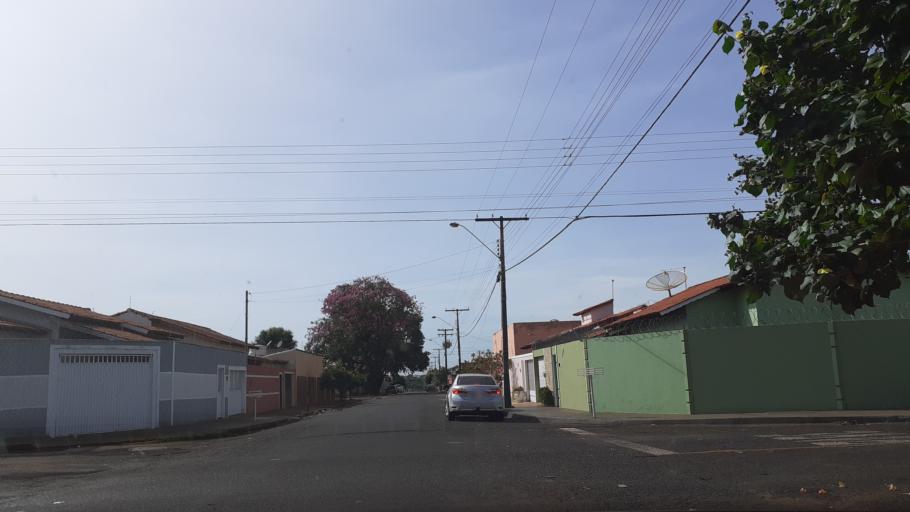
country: BR
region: Goias
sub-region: Itumbiara
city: Itumbiara
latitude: -18.4205
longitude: -49.2443
